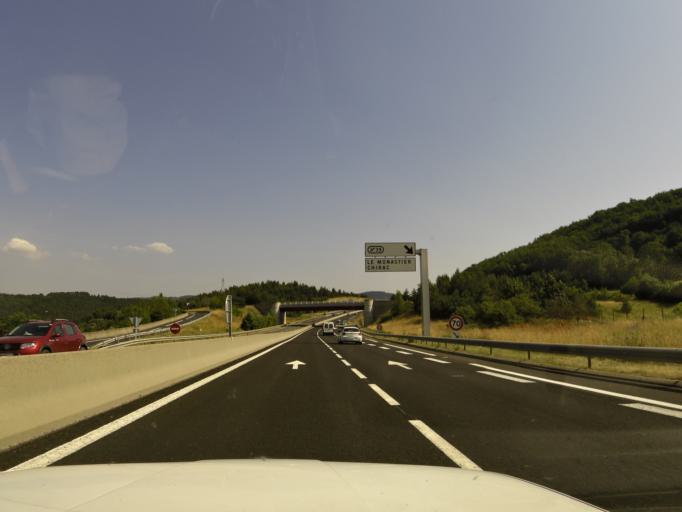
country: FR
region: Languedoc-Roussillon
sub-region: Departement de la Lozere
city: Chirac
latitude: 44.5104
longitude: 3.2425
